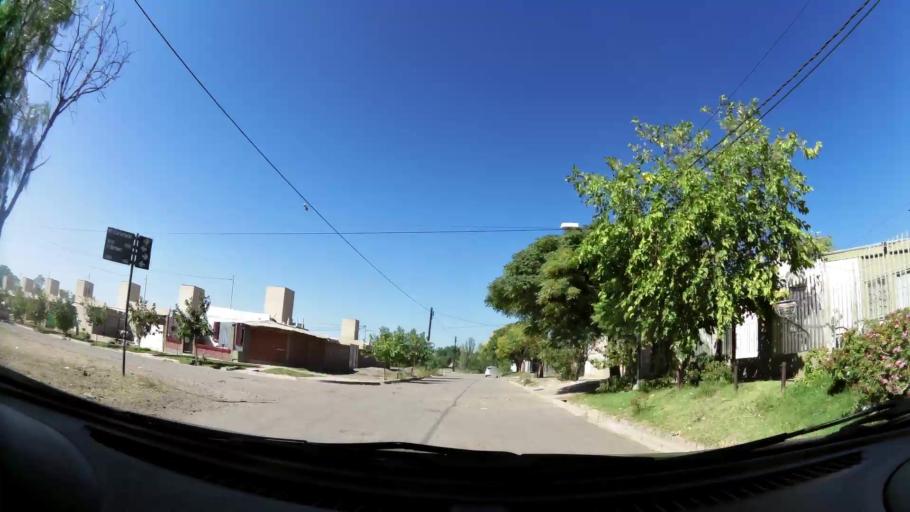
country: AR
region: Mendoza
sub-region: Departamento de Godoy Cruz
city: Godoy Cruz
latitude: -32.9058
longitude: -68.8825
